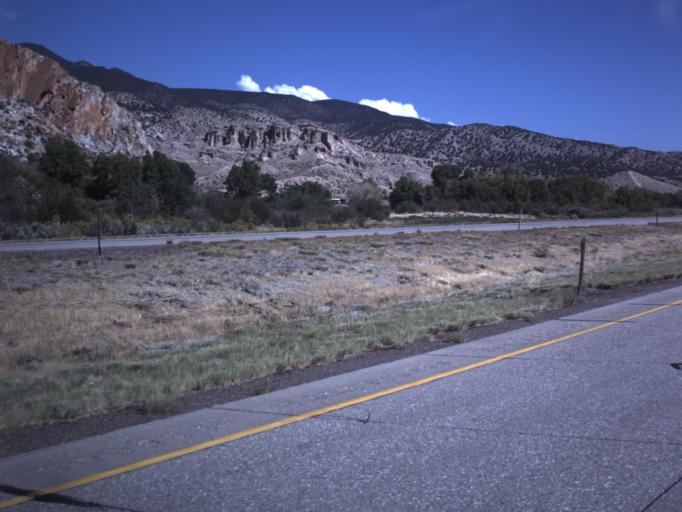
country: US
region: Utah
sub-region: Sevier County
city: Monroe
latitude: 38.5806
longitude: -112.2798
